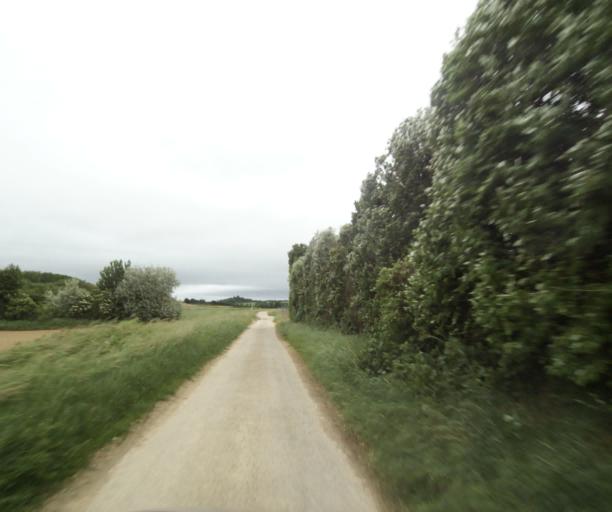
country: FR
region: Rhone-Alpes
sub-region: Departement de l'Ain
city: Miribel
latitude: 45.8446
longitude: 4.9327
